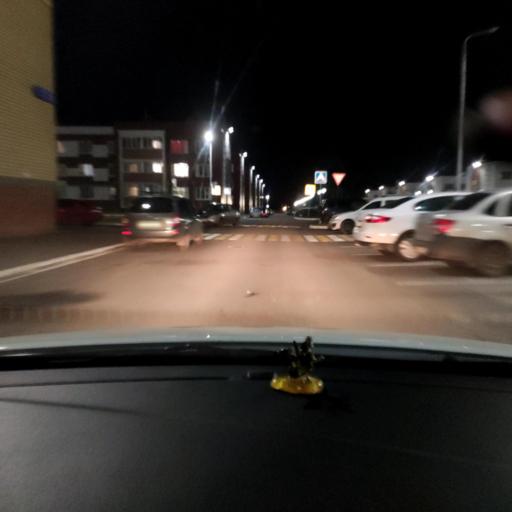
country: RU
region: Tatarstan
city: Vysokaya Gora
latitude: 55.8099
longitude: 49.4402
